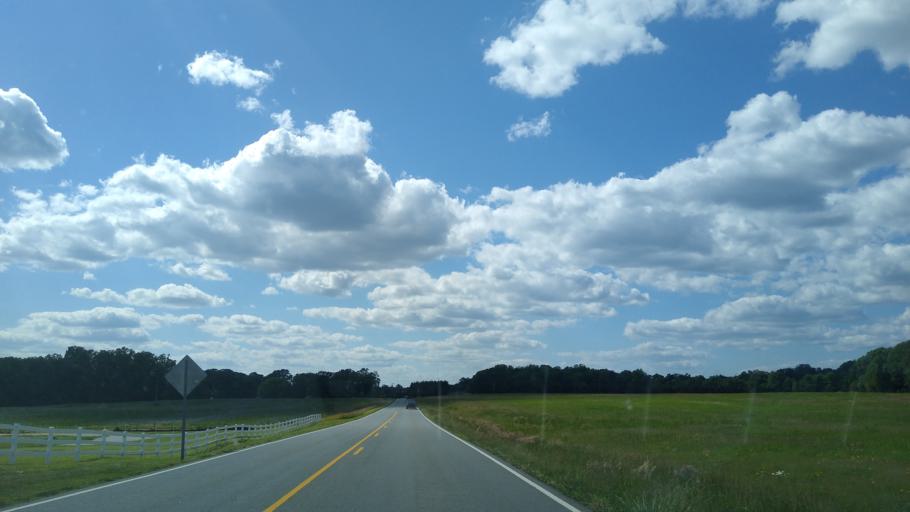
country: US
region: North Carolina
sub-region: Forsyth County
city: Kernersville
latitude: 36.0977
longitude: -80.0767
